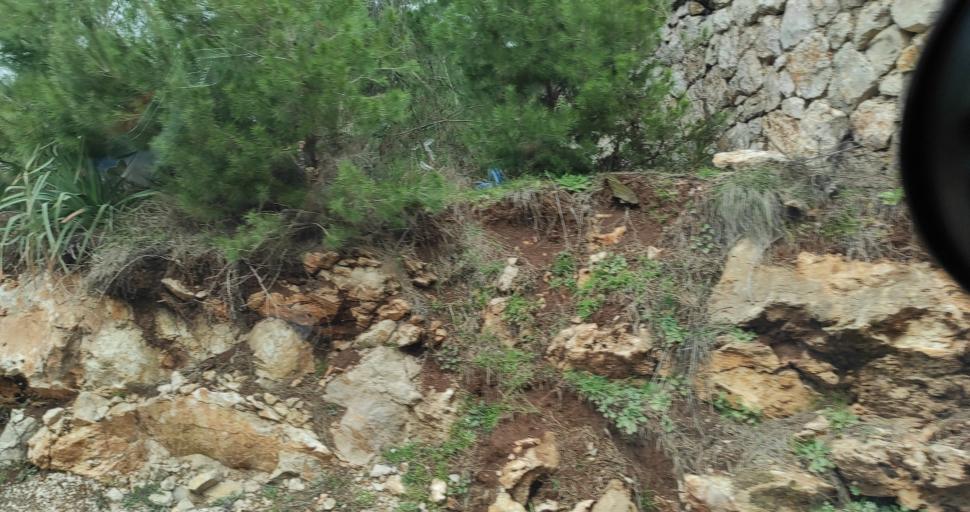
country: AL
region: Lezhe
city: Shengjin
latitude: 41.8132
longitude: 19.5747
